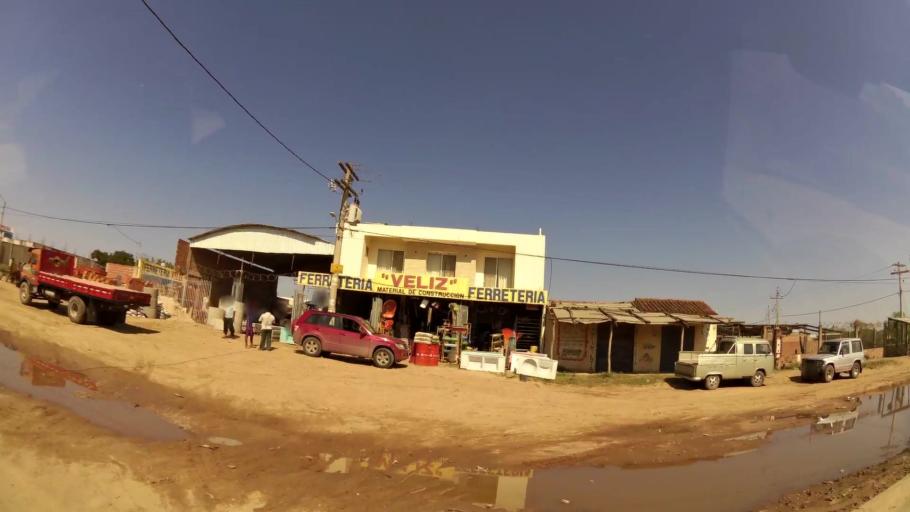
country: BO
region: Santa Cruz
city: Cotoca
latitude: -17.7287
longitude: -63.0904
